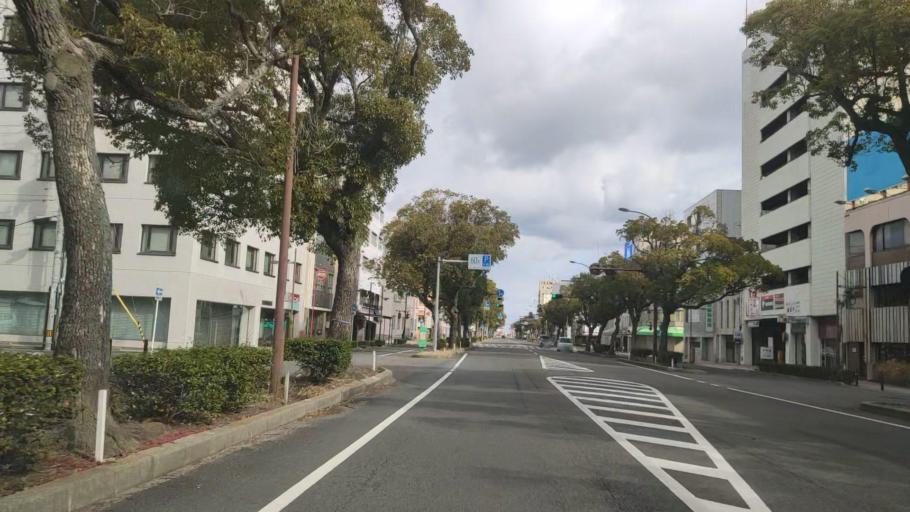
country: JP
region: Ehime
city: Saijo
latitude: 34.0674
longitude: 132.9996
